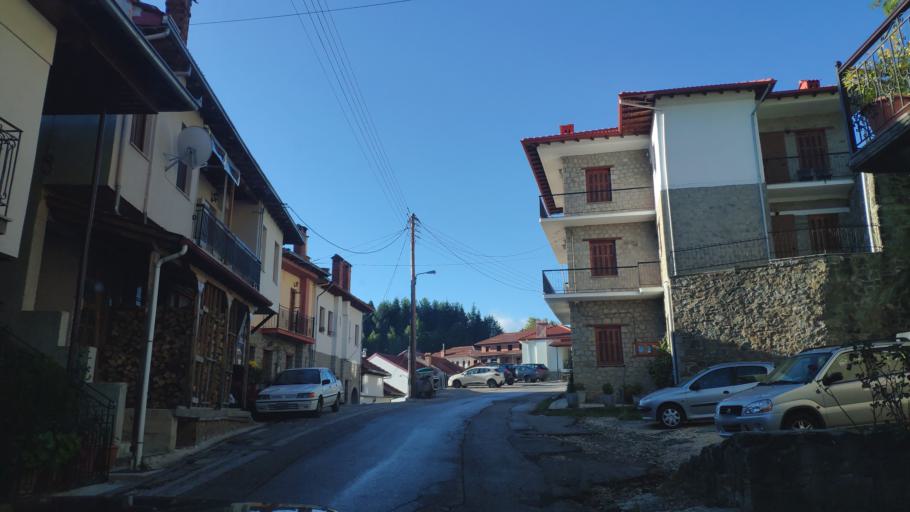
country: GR
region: Epirus
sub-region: Nomos Ioanninon
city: Metsovo
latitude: 39.7732
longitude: 21.1788
